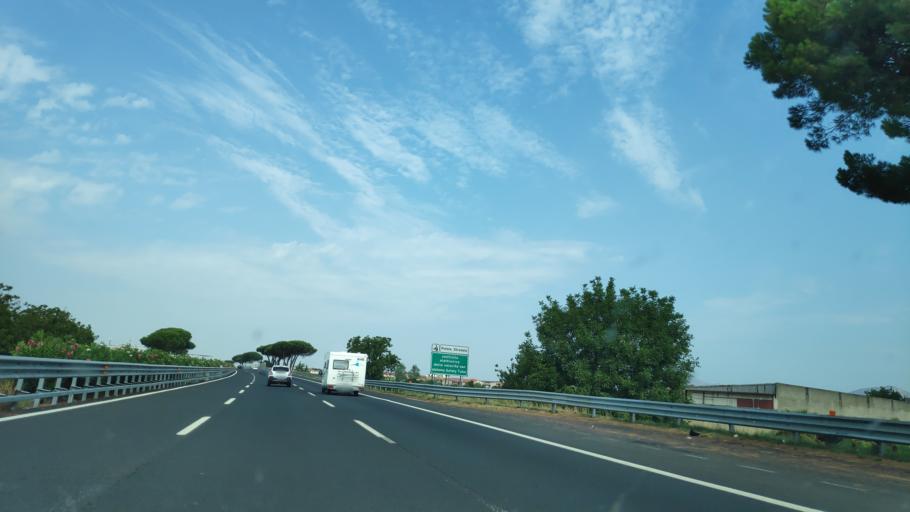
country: IT
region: Campania
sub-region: Provincia di Caserta
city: San Marco Evangelista
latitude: 41.0300
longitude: 14.3482
